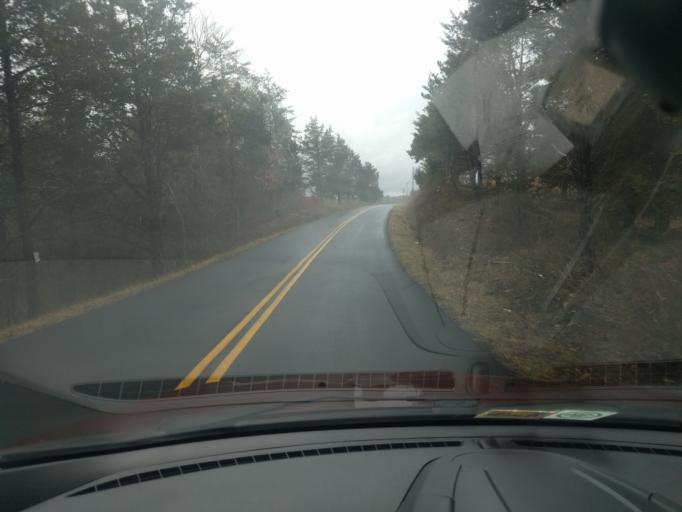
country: US
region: Virginia
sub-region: Botetourt County
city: Fincastle
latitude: 37.5308
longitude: -79.8819
